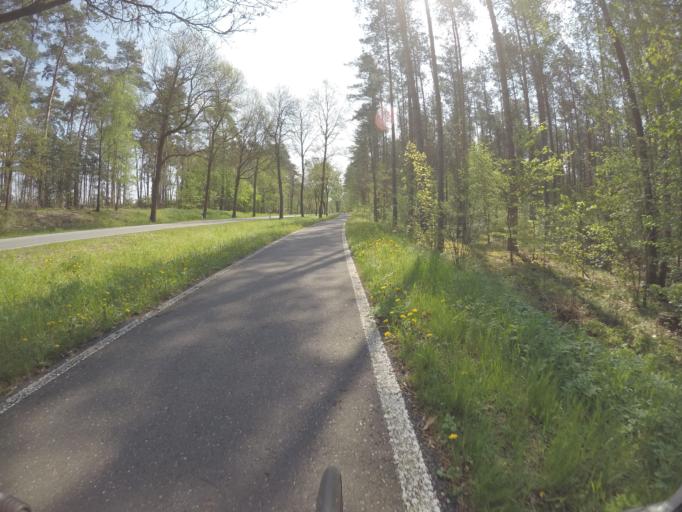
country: DE
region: Brandenburg
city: Wandlitz
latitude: 52.7947
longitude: 13.5221
